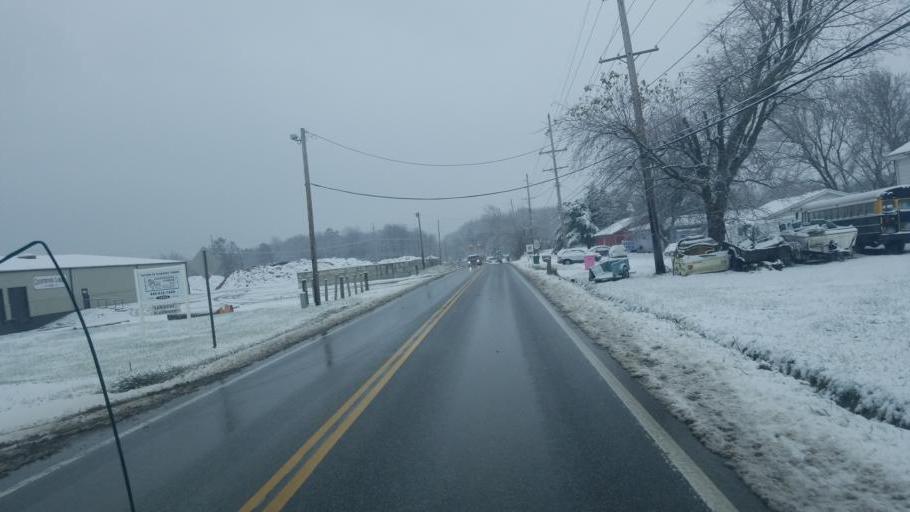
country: US
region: Ohio
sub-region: Geauga County
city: Middlefield
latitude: 41.4381
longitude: -81.0605
